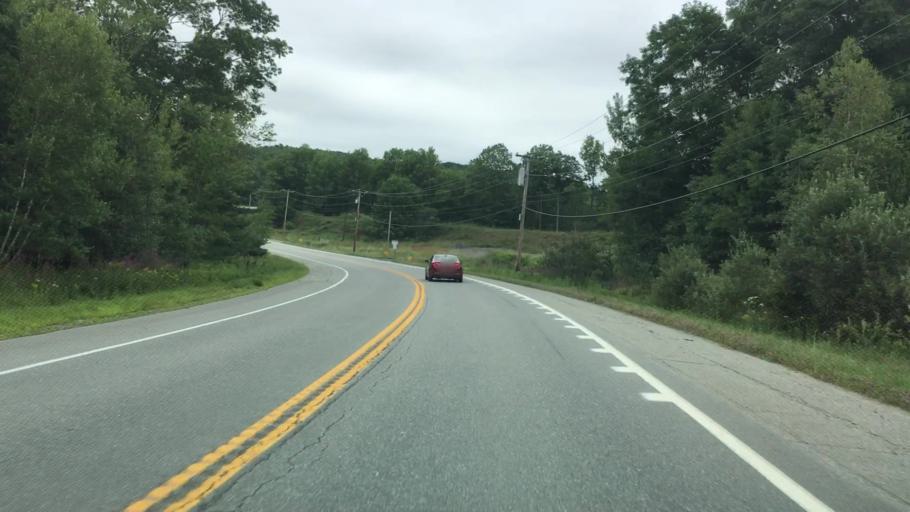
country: US
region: Maine
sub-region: Waldo County
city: Frankfort
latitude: 44.6239
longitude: -68.8691
